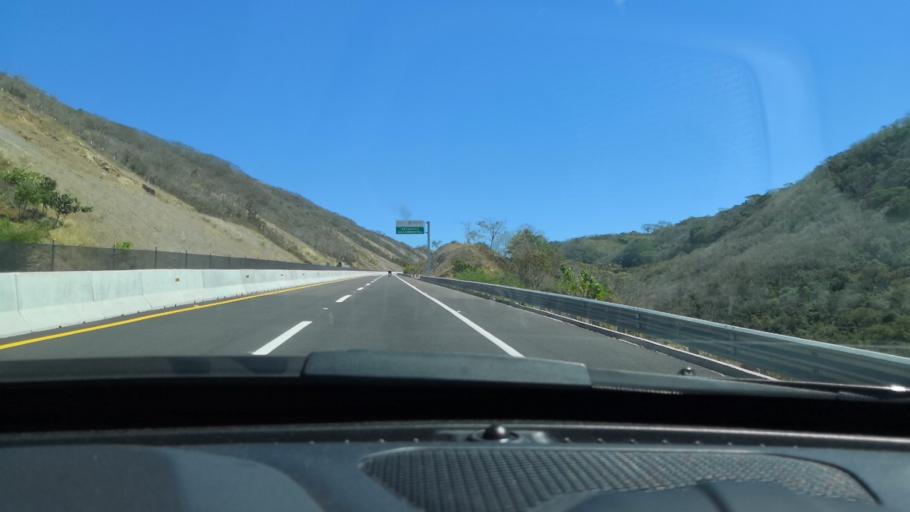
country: MX
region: Nayarit
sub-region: Compostela
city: Juan Escutia (Borbollon)
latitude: 21.1297
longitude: -104.9013
